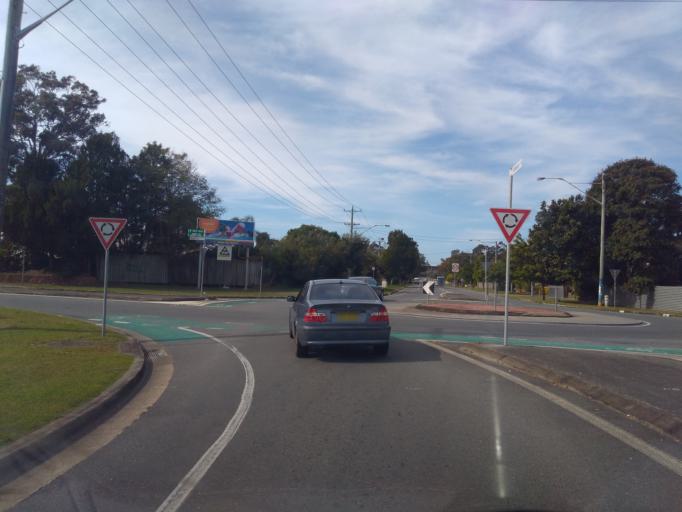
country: AU
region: New South Wales
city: Chinderah
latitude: -28.2375
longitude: 153.5590
